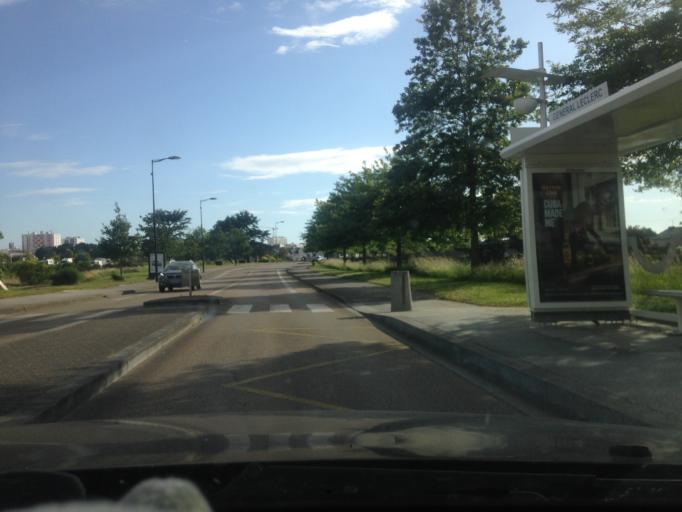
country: FR
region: Brittany
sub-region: Departement du Morbihan
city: Lanester
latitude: 47.7617
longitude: -3.3518
